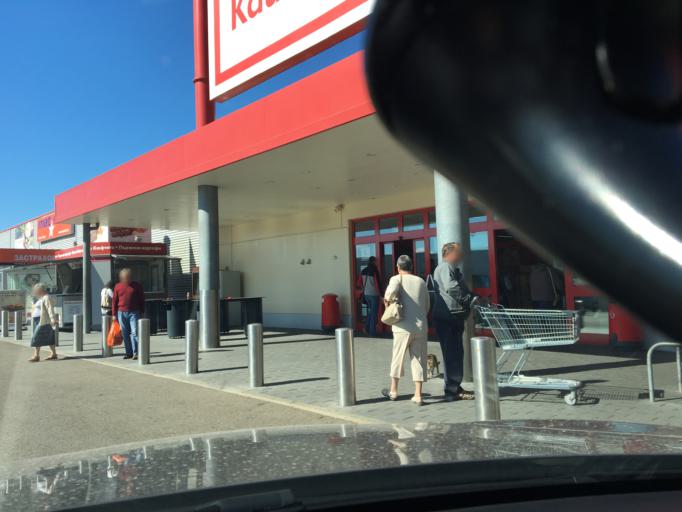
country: BG
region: Burgas
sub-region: Obshtina Burgas
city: Burgas
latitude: 42.5151
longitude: 27.4508
